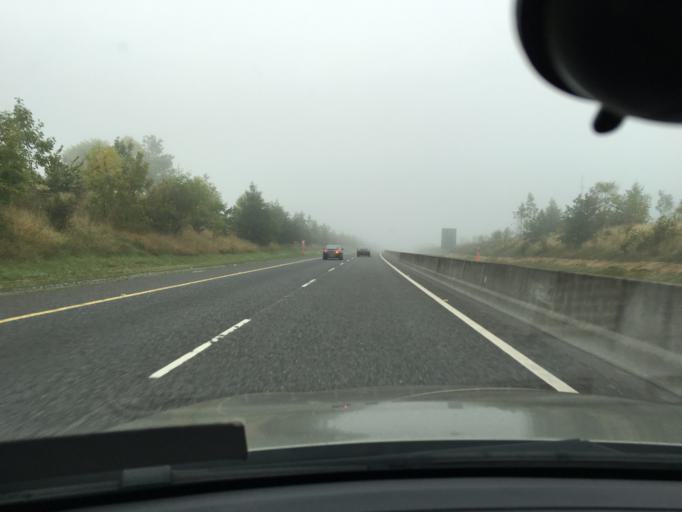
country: IE
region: Leinster
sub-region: An Iarmhi
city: Moate
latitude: 53.3943
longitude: -7.7988
